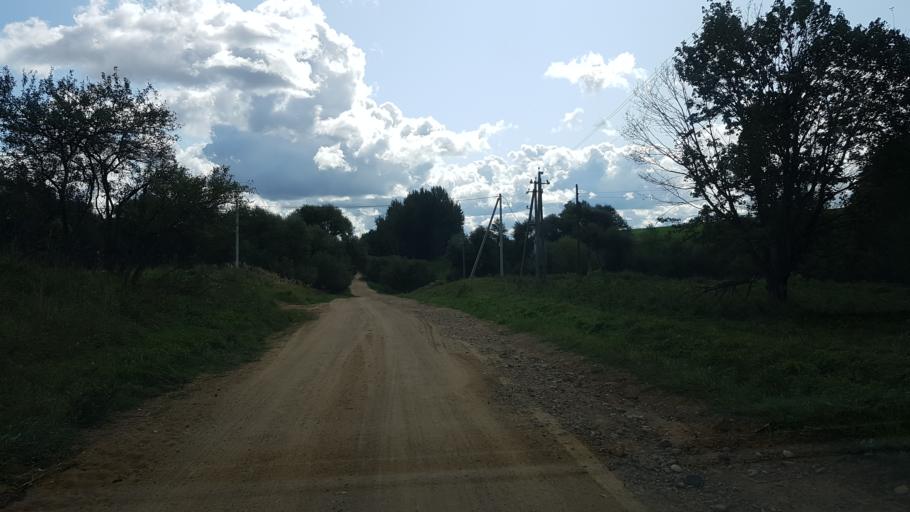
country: BY
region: Minsk
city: Dzyarzhynsk
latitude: 53.7542
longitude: 27.2070
